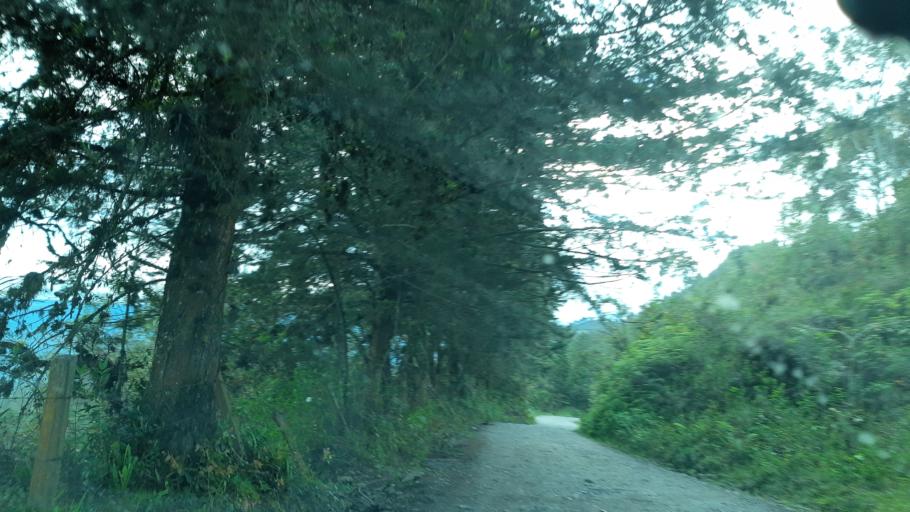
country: CO
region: Boyaca
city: Garagoa
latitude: 5.0838
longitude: -73.3192
